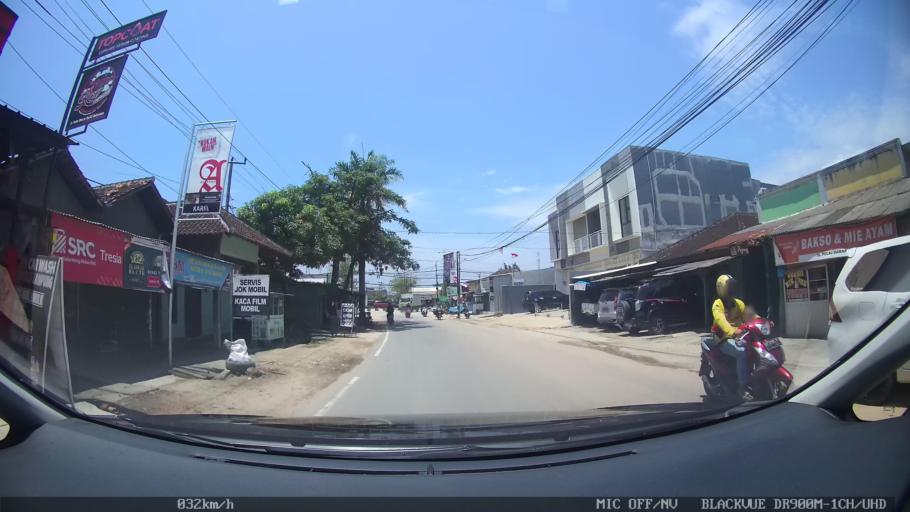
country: ID
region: Lampung
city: Kedaton
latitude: -5.3793
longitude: 105.2890
